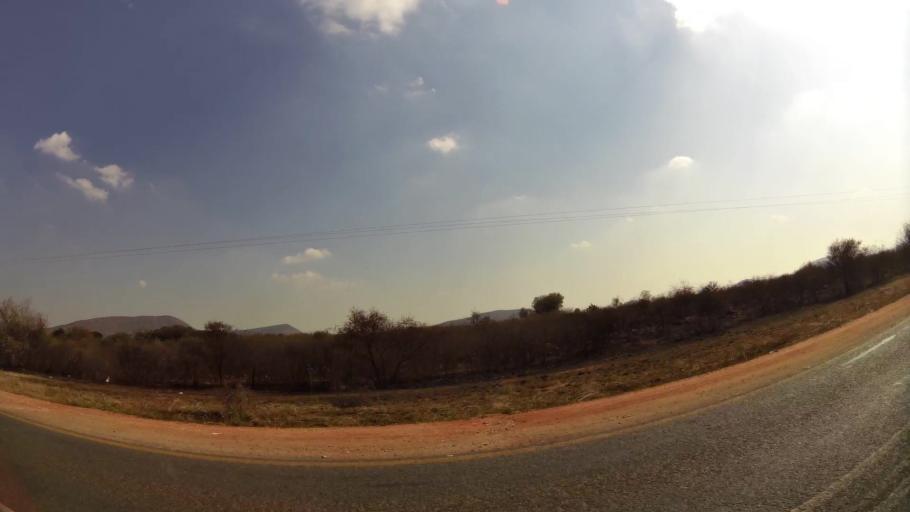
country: ZA
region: North-West
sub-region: Bojanala Platinum District Municipality
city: Mogwase
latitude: -25.4717
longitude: 27.0871
